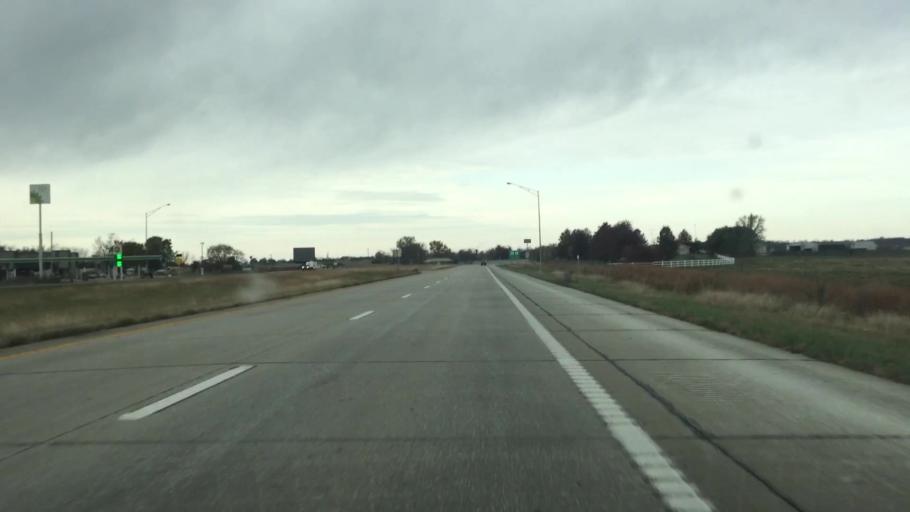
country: US
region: Missouri
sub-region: Saint Clair County
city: Osceola
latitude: 38.1414
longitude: -93.7190
